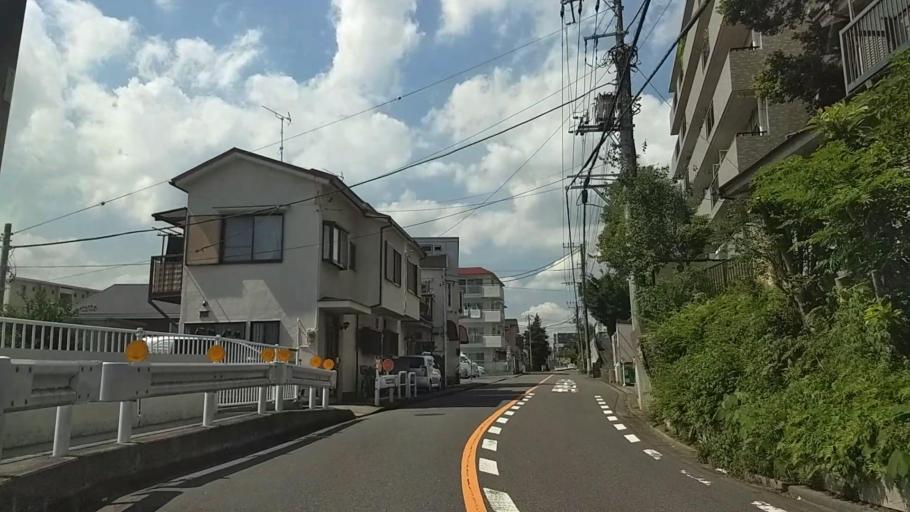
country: JP
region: Kanagawa
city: Yokohama
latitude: 35.5086
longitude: 139.5868
